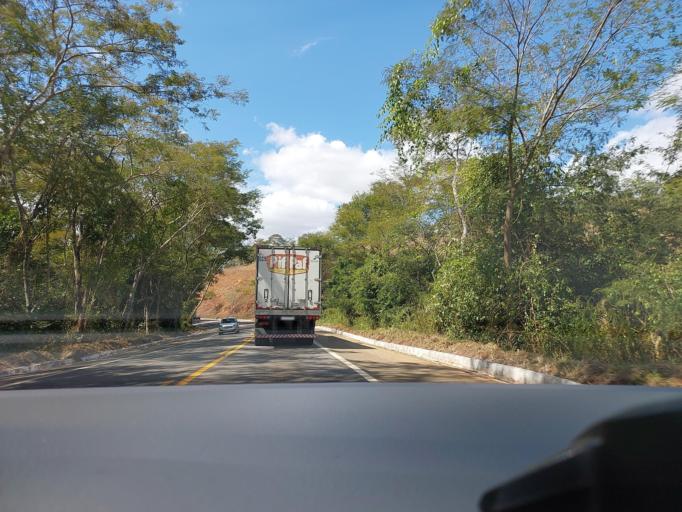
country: BR
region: Minas Gerais
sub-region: Muriae
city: Muriae
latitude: -21.1226
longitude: -42.2174
